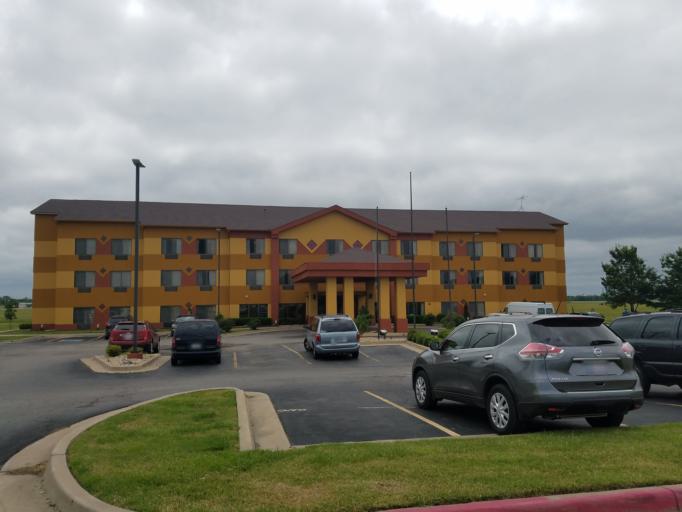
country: US
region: Oklahoma
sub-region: Mayes County
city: Chouteau
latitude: 36.2314
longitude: -95.3388
